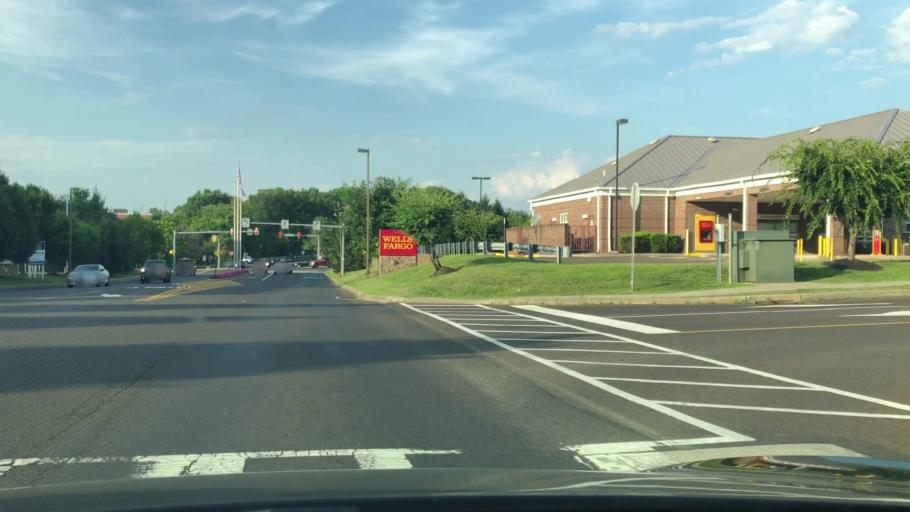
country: US
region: Pennsylvania
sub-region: Bucks County
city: Trevose
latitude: 40.1387
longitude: -74.9626
